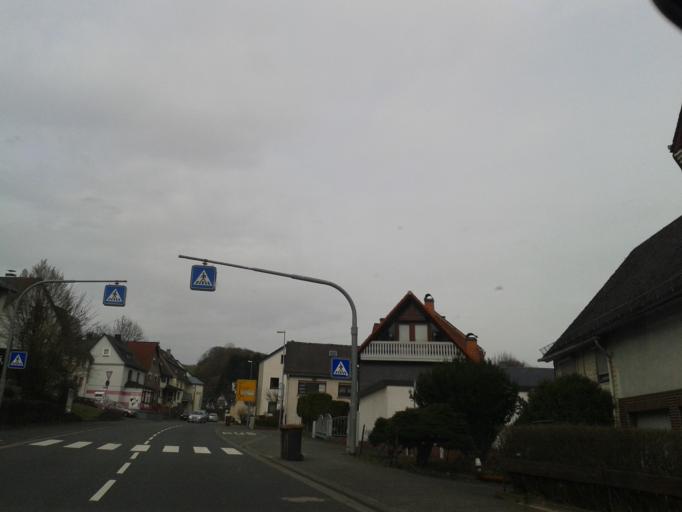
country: DE
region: Hesse
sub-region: Regierungsbezirk Giessen
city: Mittenaar
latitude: 50.7349
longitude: 8.3445
